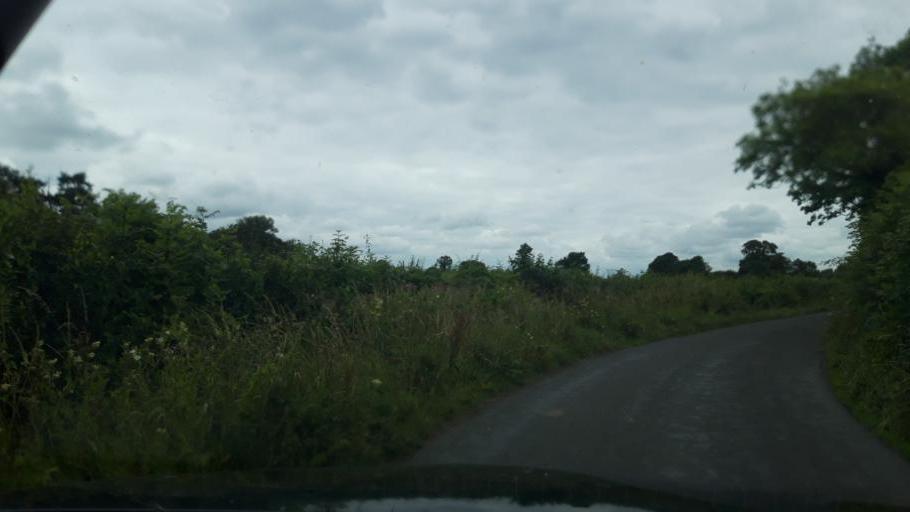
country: IE
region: Leinster
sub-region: Kilkenny
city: Graiguenamanagh
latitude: 52.5955
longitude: -7.0303
